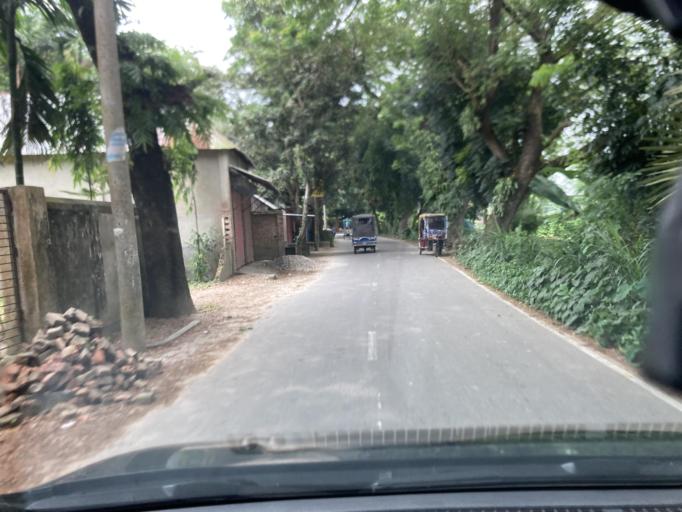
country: BD
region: Dhaka
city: Dohar
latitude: 23.7899
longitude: 90.0614
